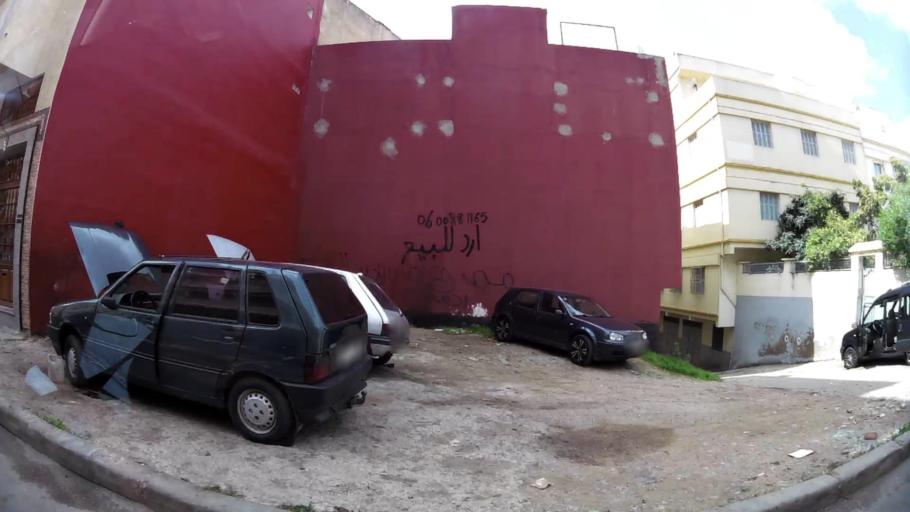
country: MA
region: Tanger-Tetouan
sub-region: Tanger-Assilah
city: Tangier
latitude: 35.7582
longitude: -5.8158
